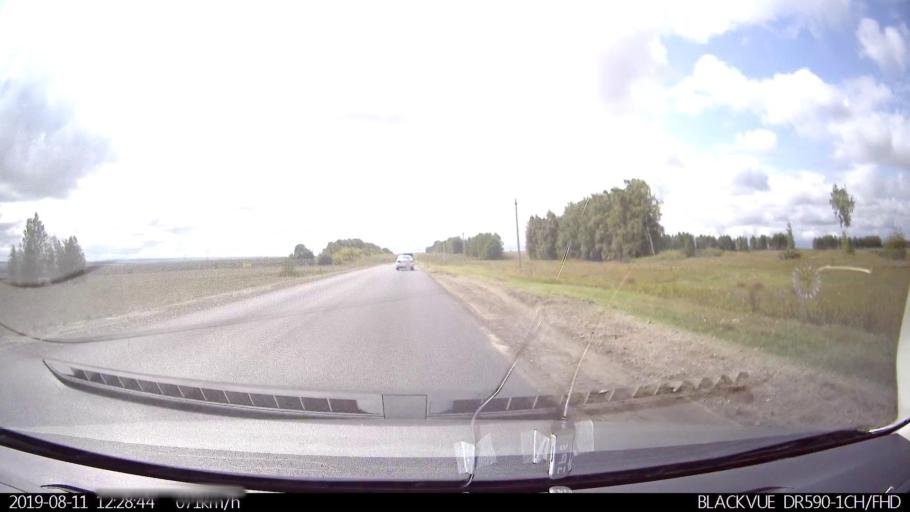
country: RU
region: Ulyanovsk
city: Ignatovka
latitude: 53.8408
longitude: 47.9091
